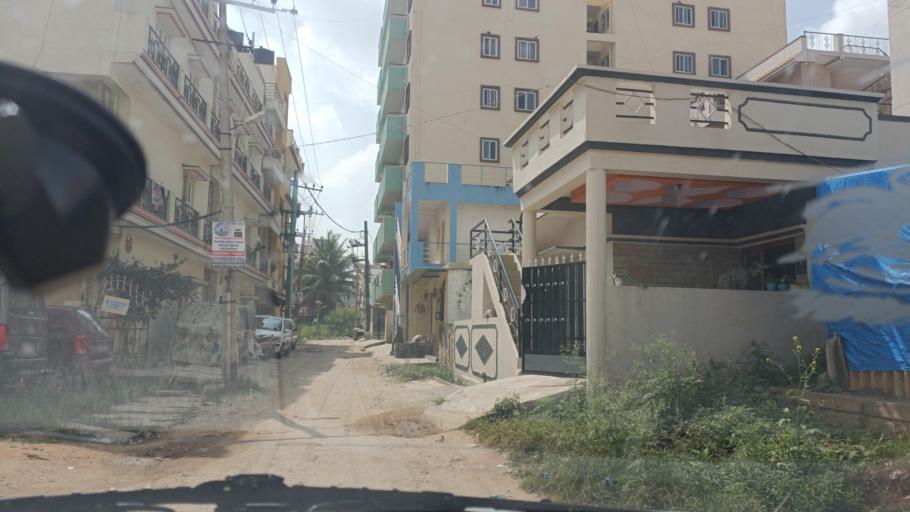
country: IN
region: Karnataka
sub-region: Bangalore Urban
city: Yelahanka
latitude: 13.1463
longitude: 77.6202
